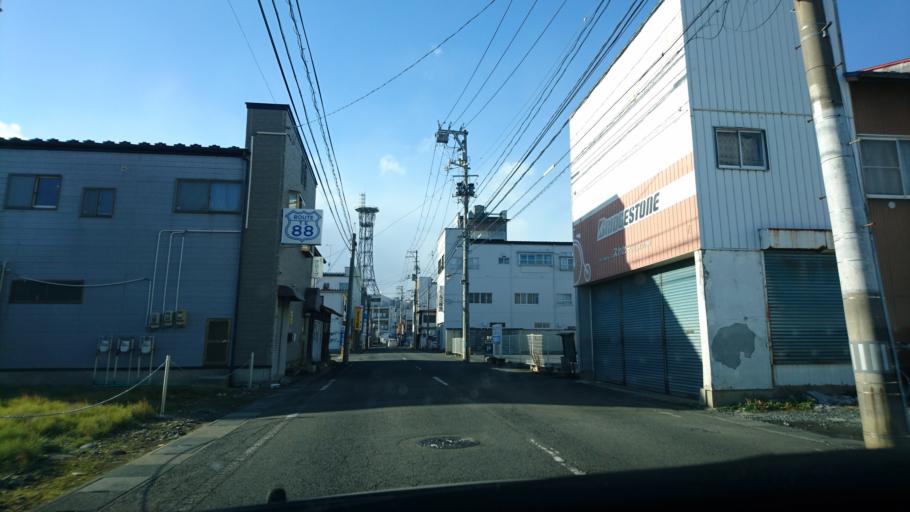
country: JP
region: Iwate
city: Mizusawa
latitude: 39.1416
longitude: 141.1453
